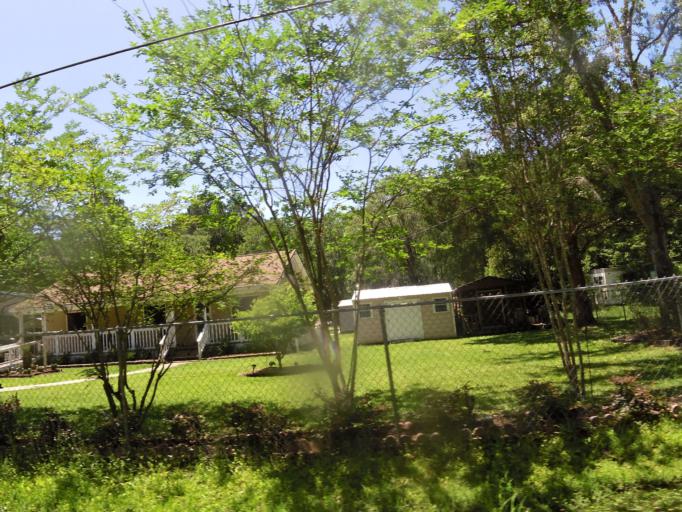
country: US
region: Florida
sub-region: Bradford County
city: Starke
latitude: 29.9521
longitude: -82.0903
